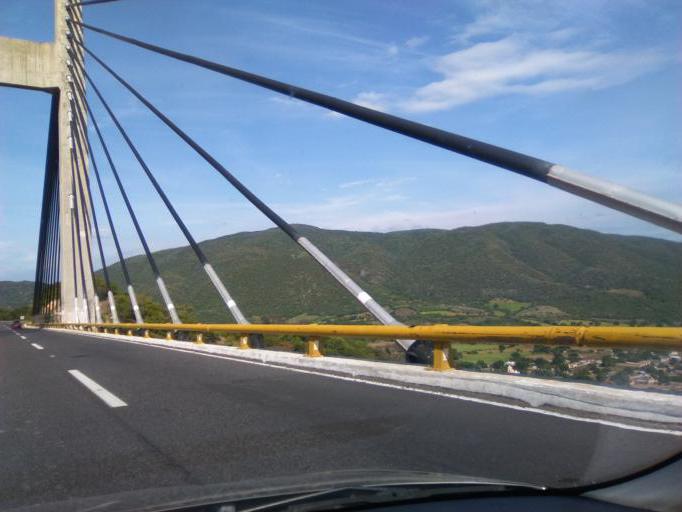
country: MX
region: Guerrero
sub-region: Huitzuco de los Figueroa
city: Ciudad de Huitzuco
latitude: 18.3331
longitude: -99.1935
